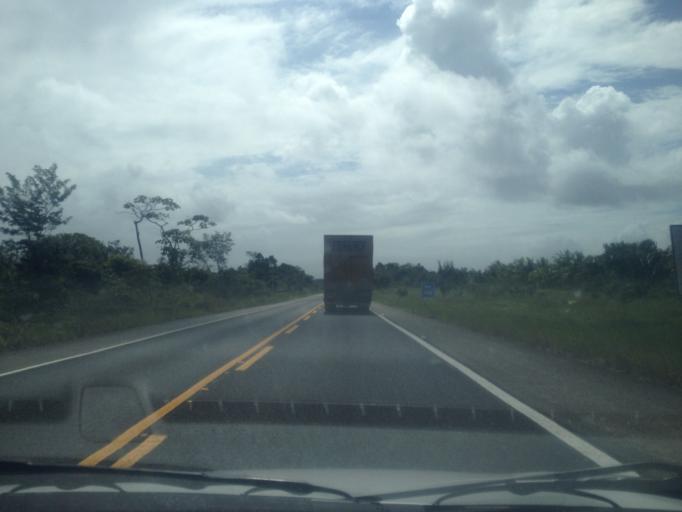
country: BR
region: Bahia
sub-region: Conde
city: Conde
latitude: -11.7399
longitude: -37.5793
